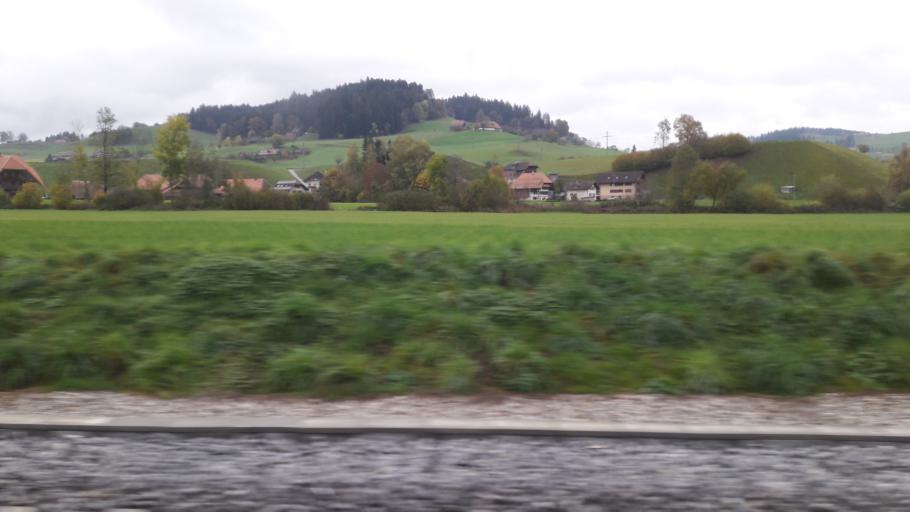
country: CH
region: Bern
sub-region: Emmental District
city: Trachselwald
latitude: 47.0098
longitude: 7.7241
